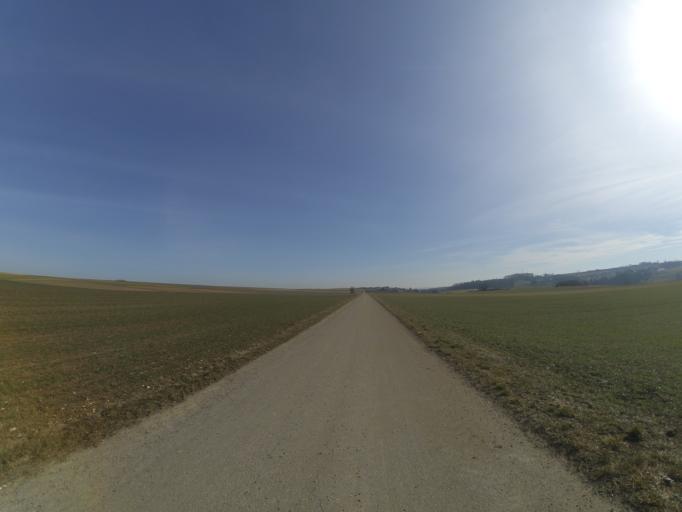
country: DE
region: Baden-Wuerttemberg
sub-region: Tuebingen Region
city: Bernstadt
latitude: 48.4873
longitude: 10.0348
